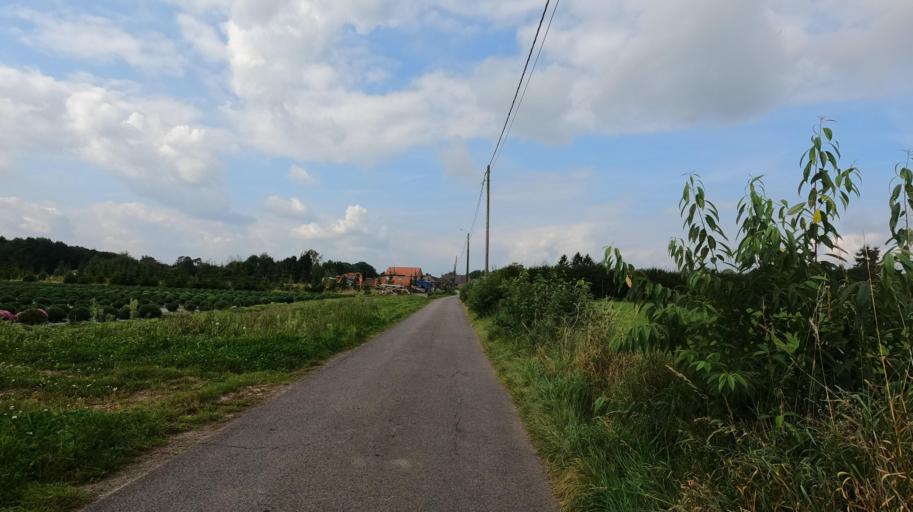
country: BE
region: Flanders
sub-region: Provincie Vlaams-Brabant
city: Keerbergen
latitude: 51.0240
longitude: 4.6645
